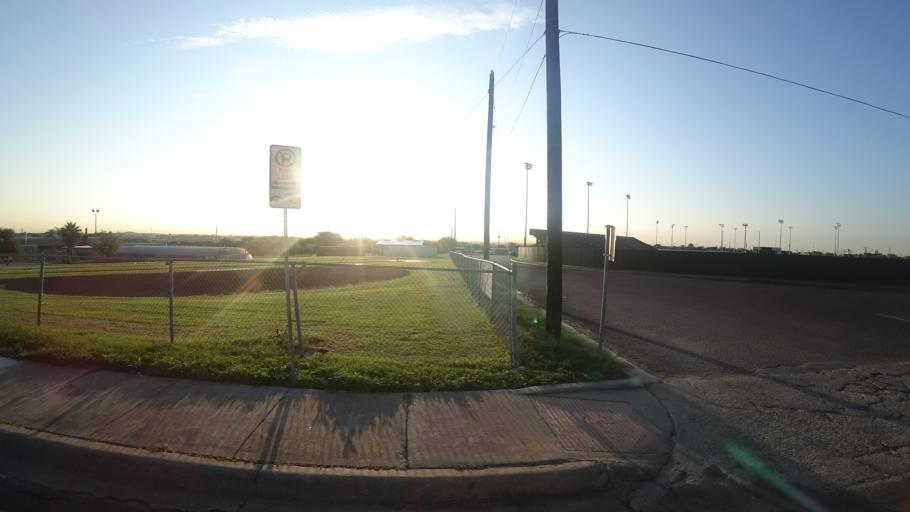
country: US
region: Texas
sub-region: Travis County
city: Austin
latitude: 30.3256
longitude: -97.6887
